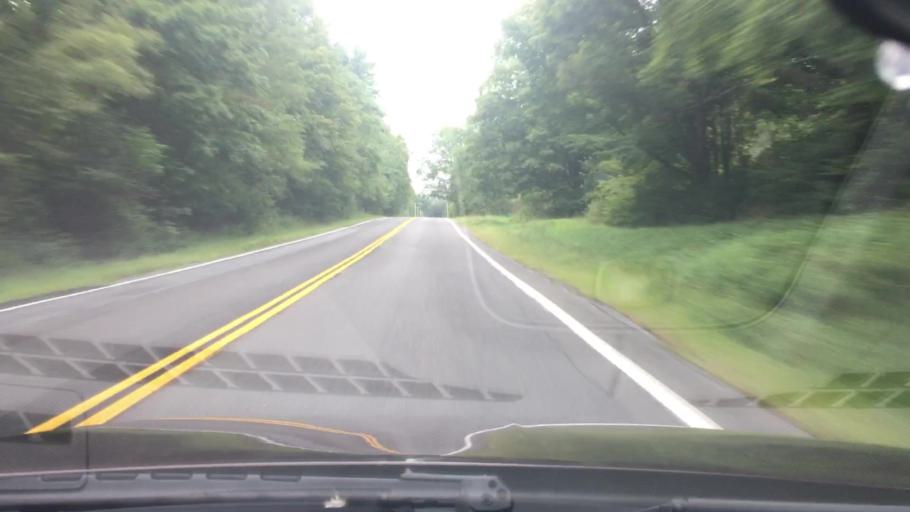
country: US
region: New York
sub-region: Dutchess County
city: Millbrook
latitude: 41.7858
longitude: -73.7298
